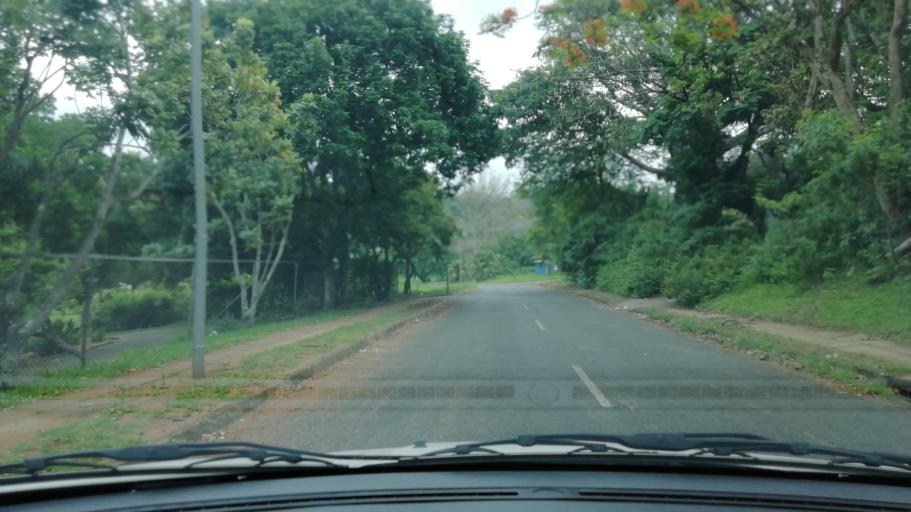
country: ZA
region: KwaZulu-Natal
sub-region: uThungulu District Municipality
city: Empangeni
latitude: -28.7536
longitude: 31.8913
